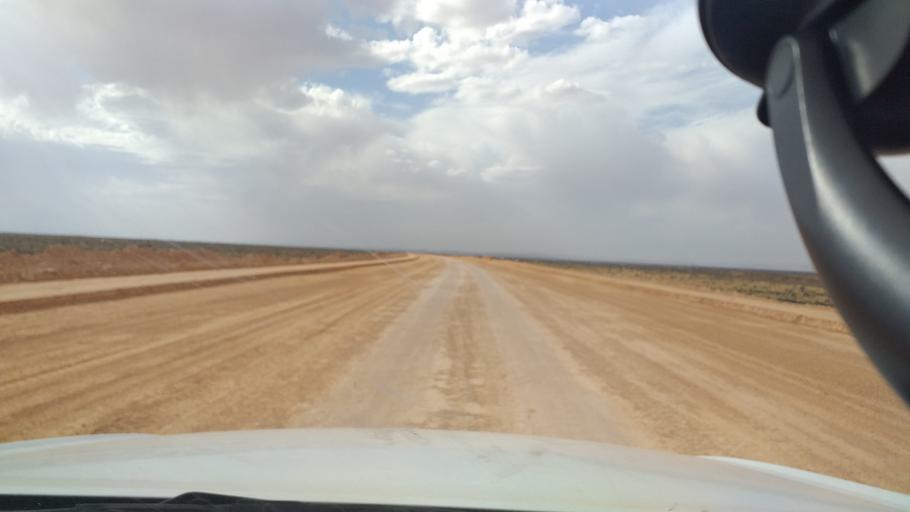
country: TN
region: Madanin
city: Medenine
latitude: 33.2829
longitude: 10.5967
